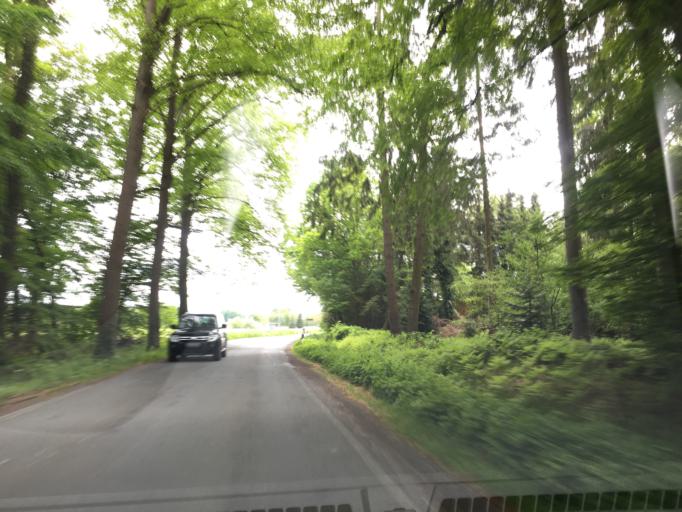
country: DE
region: North Rhine-Westphalia
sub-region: Regierungsbezirk Munster
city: Havixbeck
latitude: 51.9776
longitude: 7.4699
